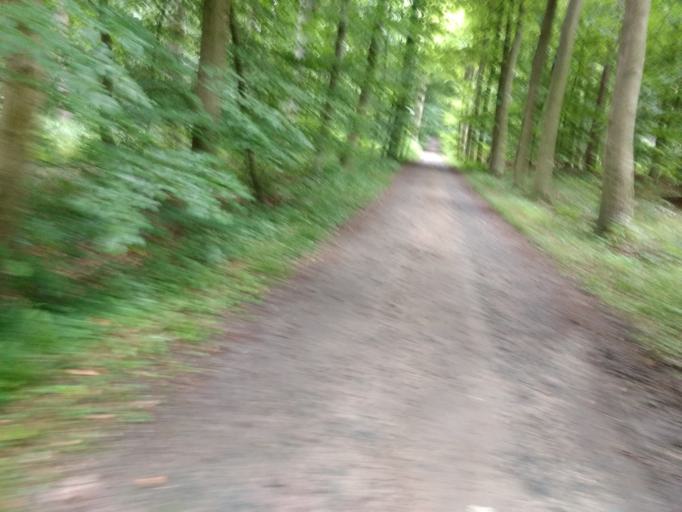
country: BE
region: Flanders
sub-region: Provincie Vlaams-Brabant
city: Bierbeek
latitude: 50.8066
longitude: 4.7136
